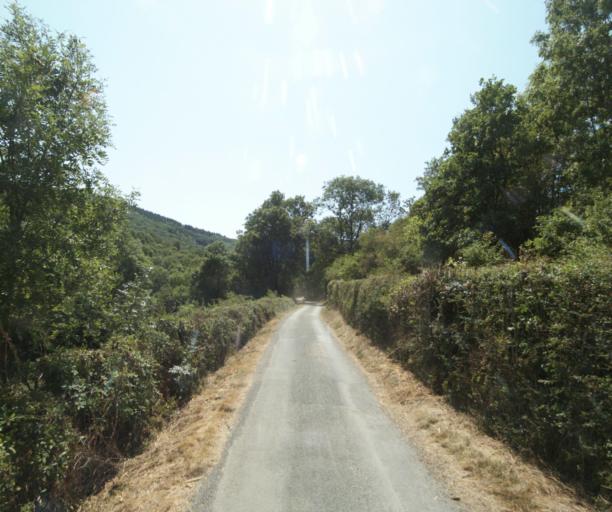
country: FR
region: Rhone-Alpes
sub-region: Departement du Rhone
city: Saint-Pierre-la-Palud
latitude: 45.7897
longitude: 4.6238
